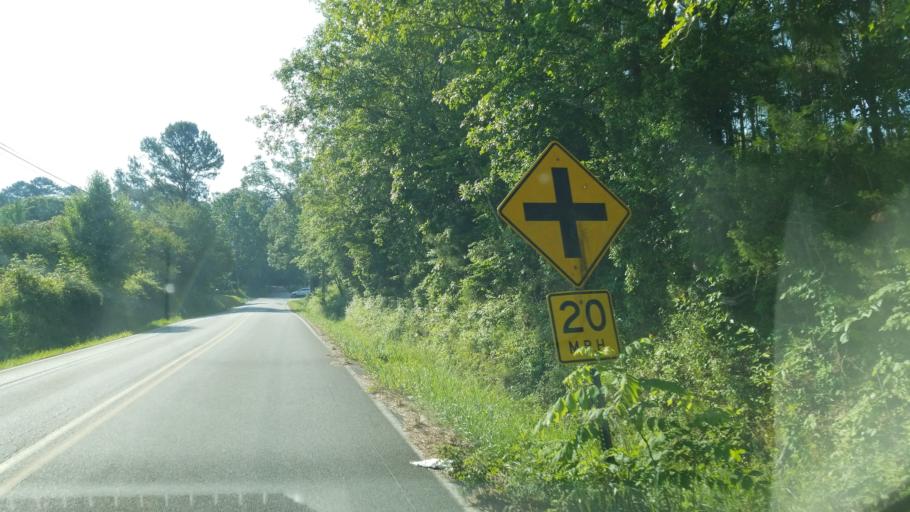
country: US
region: Tennessee
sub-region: Hamilton County
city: Collegedale
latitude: 35.0770
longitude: -85.0003
